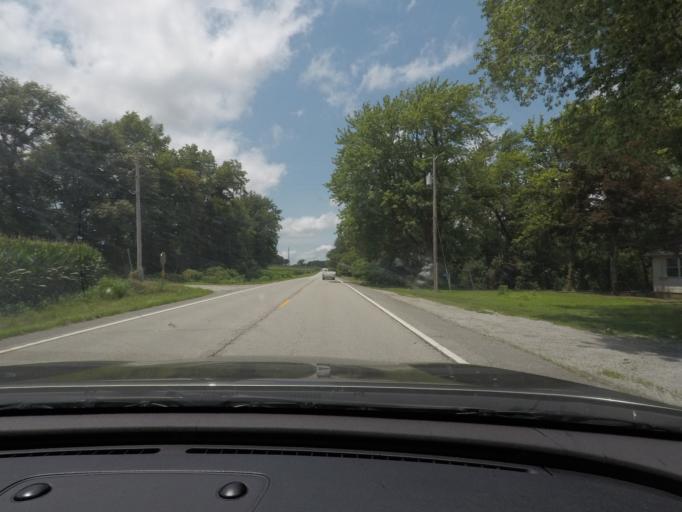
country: US
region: Missouri
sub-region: Carroll County
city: Carrollton
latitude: 39.1998
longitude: -93.4353
